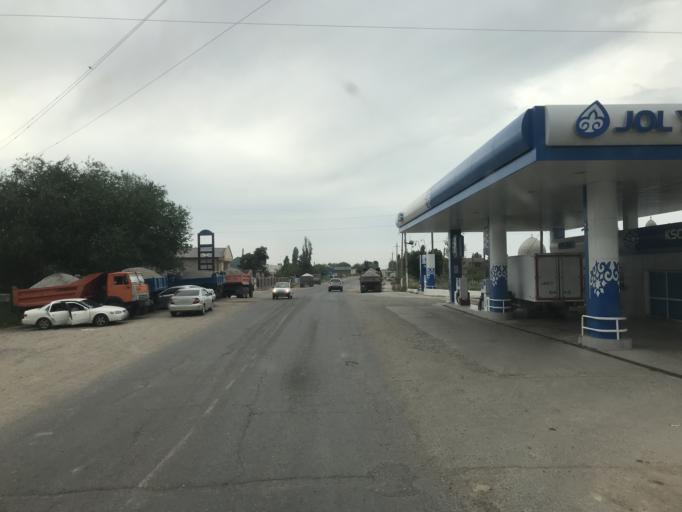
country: KZ
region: Ongtustik Qazaqstan
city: Asykata
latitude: 40.9010
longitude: 68.3590
